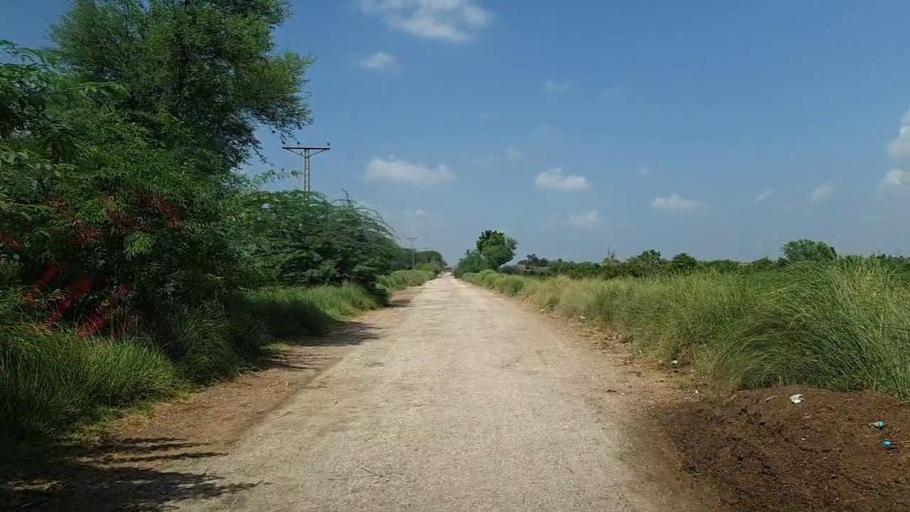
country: PK
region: Sindh
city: Kandiaro
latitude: 26.9982
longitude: 68.2540
